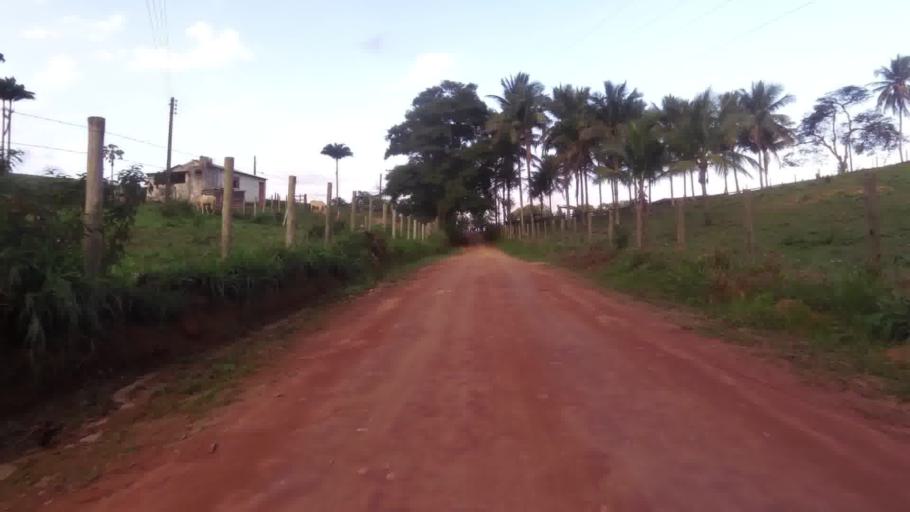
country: BR
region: Espirito Santo
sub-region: Guarapari
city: Guarapari
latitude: -20.6782
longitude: -40.6216
